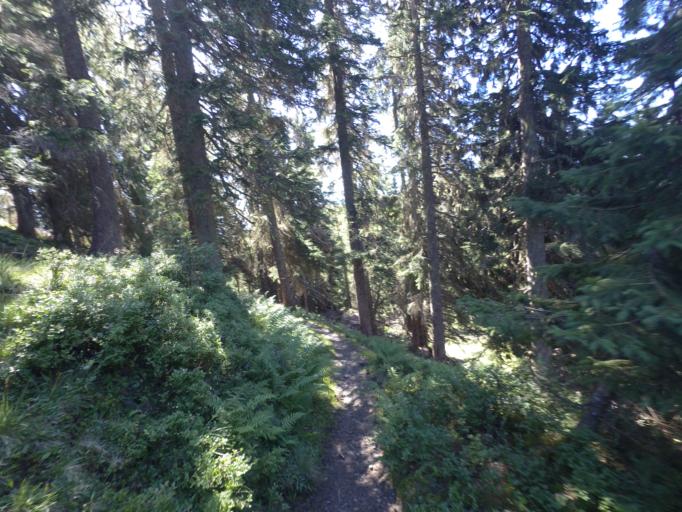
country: AT
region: Salzburg
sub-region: Politischer Bezirk Sankt Johann im Pongau
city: Goldegg
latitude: 47.3599
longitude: 13.0696
